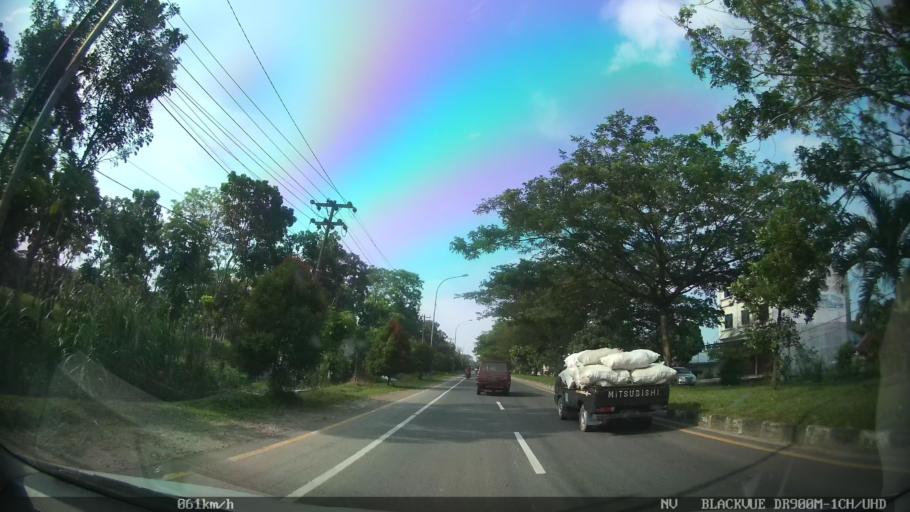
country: ID
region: North Sumatra
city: Percut
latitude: 3.5831
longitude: 98.8031
